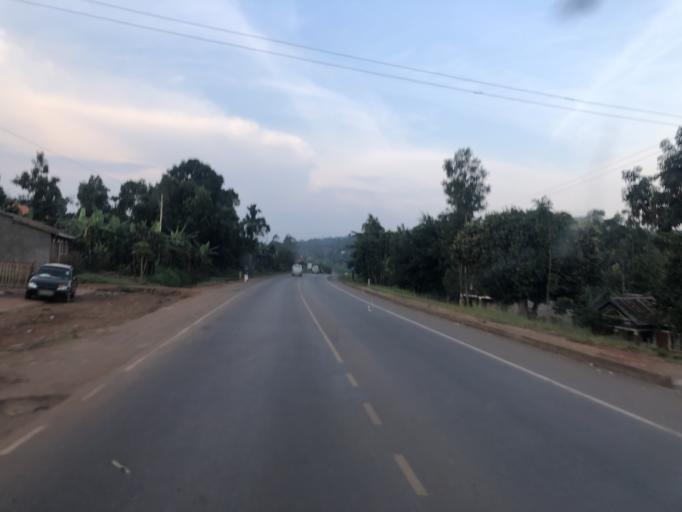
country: UG
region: Central Region
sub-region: Mpigi District
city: Mpigi
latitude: 0.2231
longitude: 32.3373
